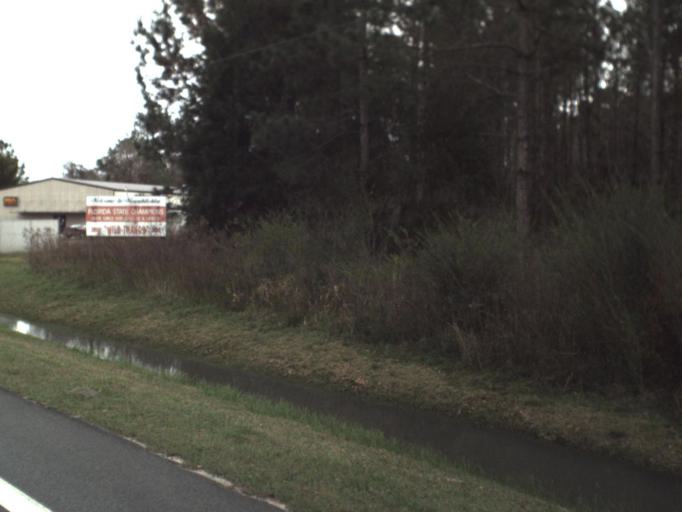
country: US
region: Florida
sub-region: Gulf County
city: Wewahitchka
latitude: 30.1191
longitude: -85.2113
